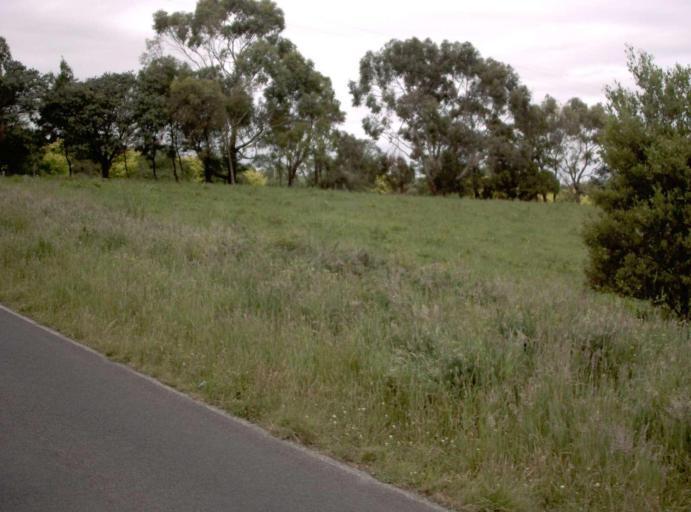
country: AU
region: Victoria
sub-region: Bass Coast
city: North Wonthaggi
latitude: -38.4465
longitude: 145.8020
